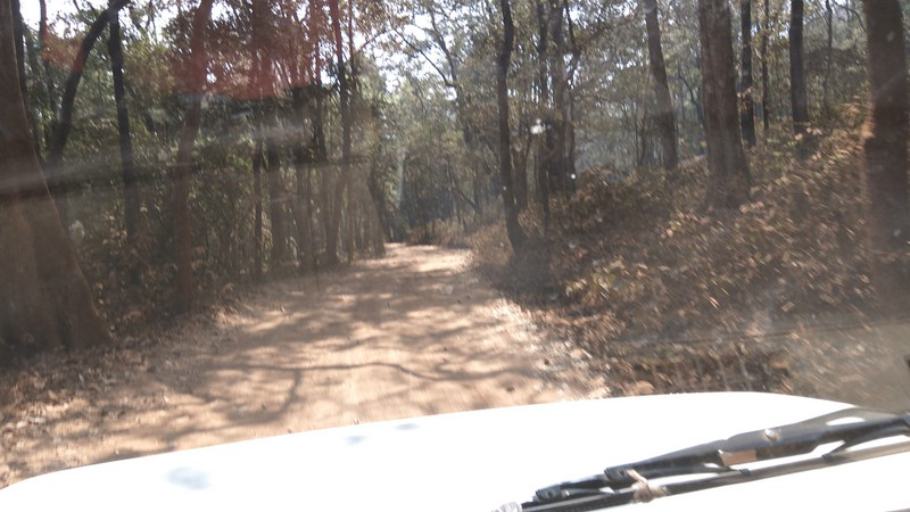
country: IN
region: Goa
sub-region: South Goa
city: Sanguem
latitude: 15.3280
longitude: 74.2815
